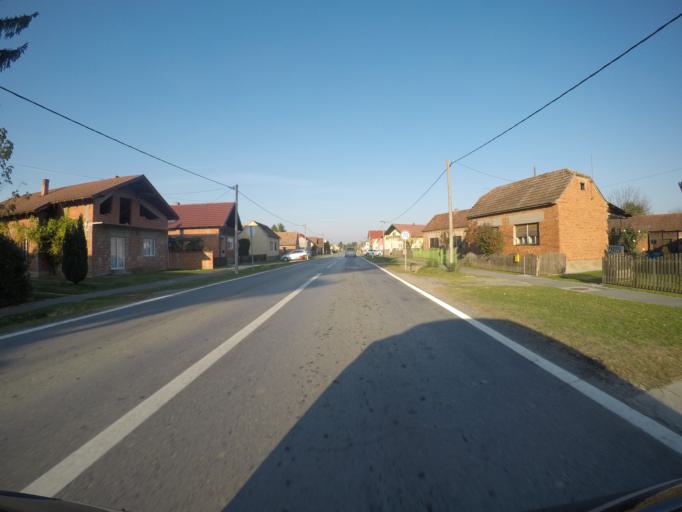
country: HU
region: Somogy
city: Barcs
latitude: 45.9103
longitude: 17.4421
